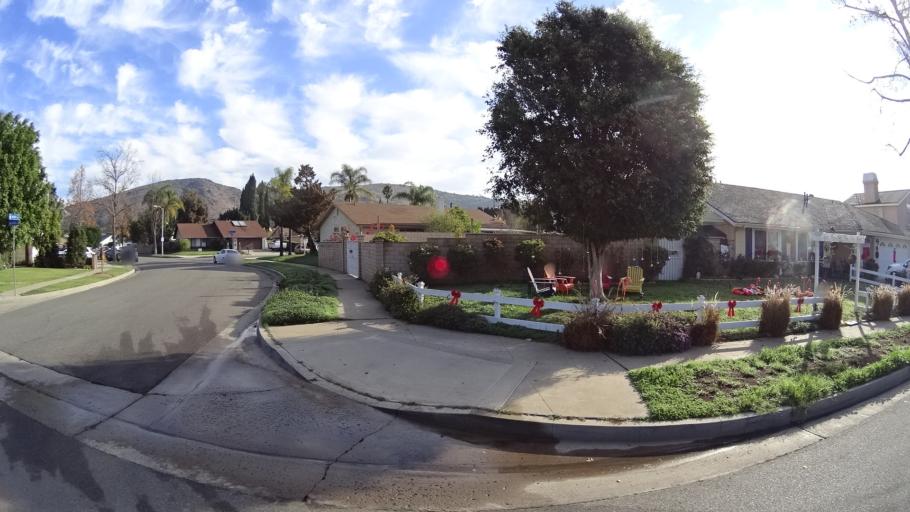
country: US
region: California
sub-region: Orange County
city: Villa Park
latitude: 33.7958
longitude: -117.8030
